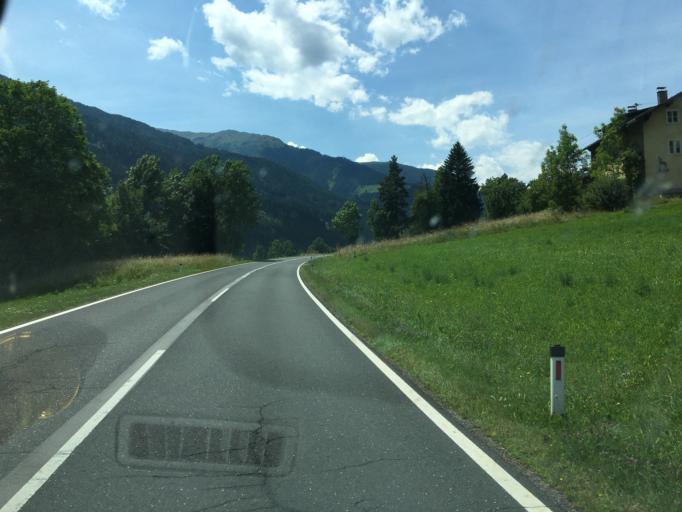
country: AT
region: Carinthia
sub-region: Politischer Bezirk Spittal an der Drau
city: Rangersdorf
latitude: 46.8627
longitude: 12.9670
